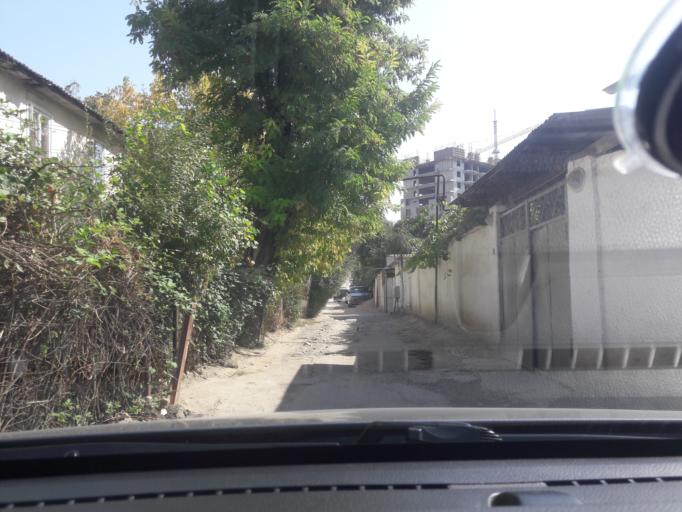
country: TJ
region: Dushanbe
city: Dushanbe
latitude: 38.5768
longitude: 68.7994
